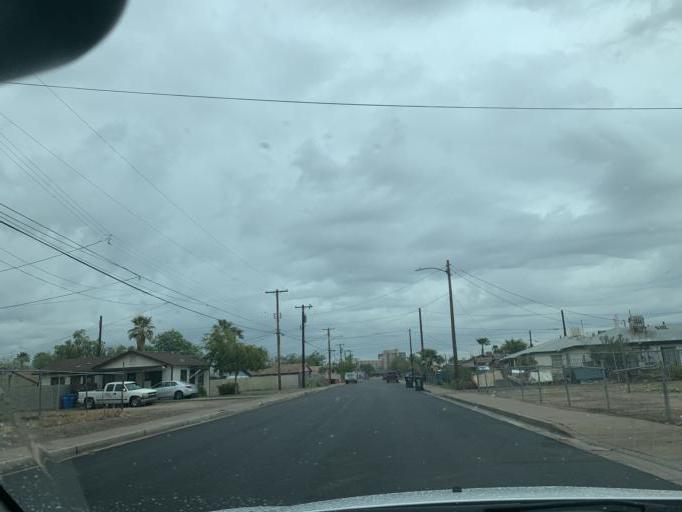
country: US
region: Arizona
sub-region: Maricopa County
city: Phoenix
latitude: 33.4534
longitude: -112.0513
